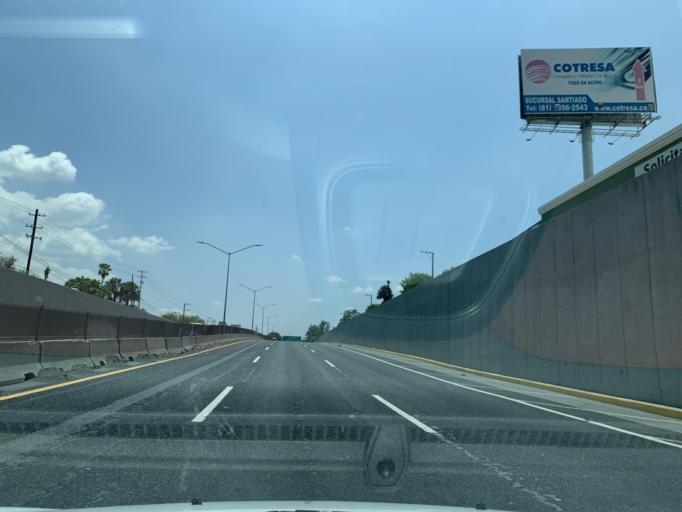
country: MX
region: Nuevo Leon
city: Santiago
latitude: 25.4310
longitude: -100.1516
